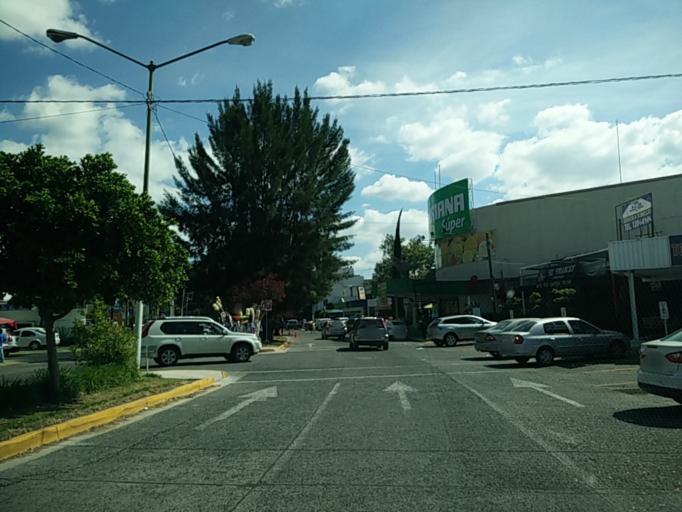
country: MX
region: Jalisco
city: Guadalajara
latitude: 20.6675
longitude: -103.4048
